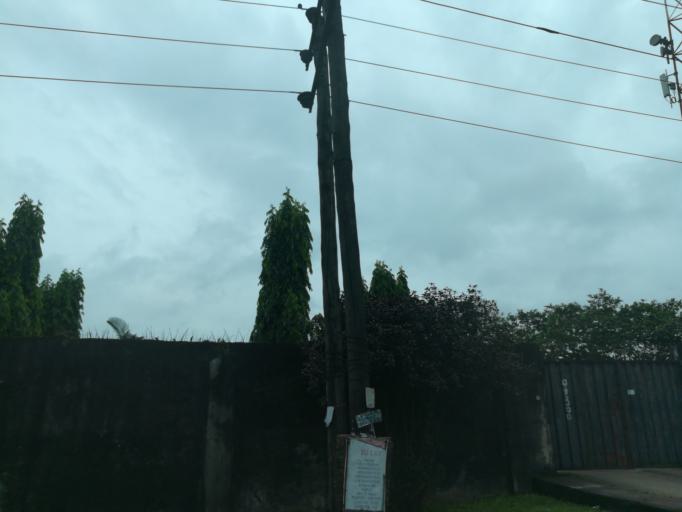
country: NG
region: Rivers
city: Port Harcourt
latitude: 4.8292
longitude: 7.0222
